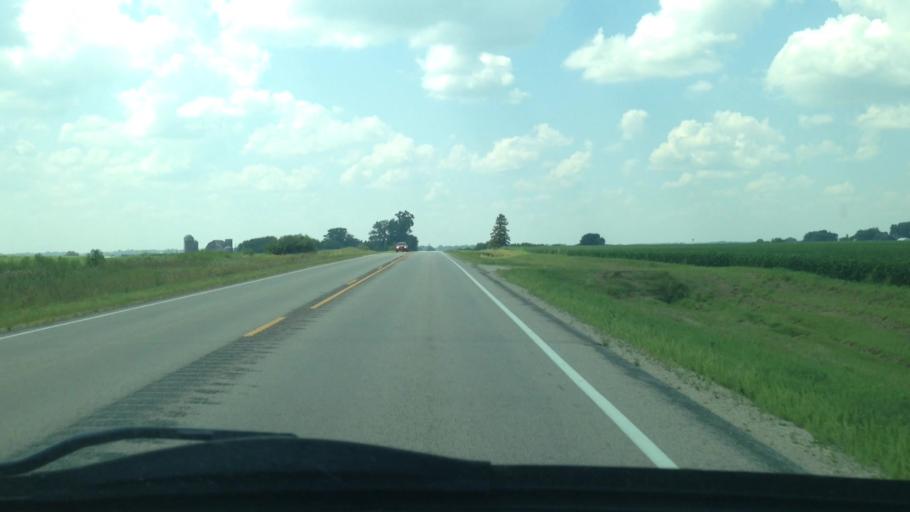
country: US
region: Minnesota
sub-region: Olmsted County
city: Stewartville
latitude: 43.8555
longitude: -92.4240
